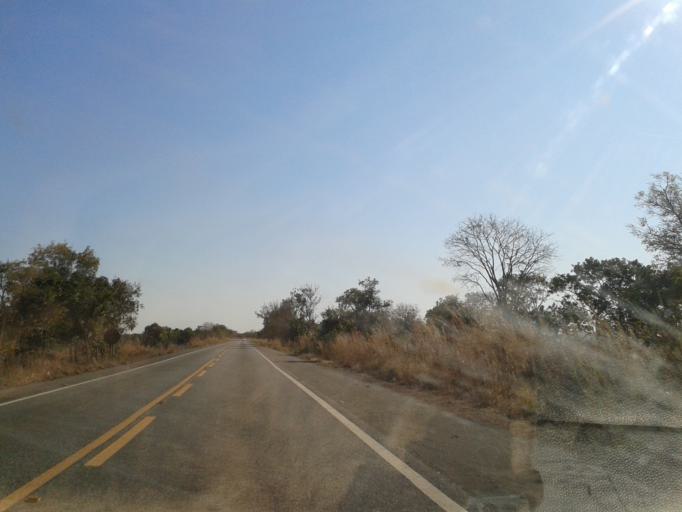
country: BR
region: Goias
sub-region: Mozarlandia
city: Mozarlandia
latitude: -14.9231
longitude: -50.5536
